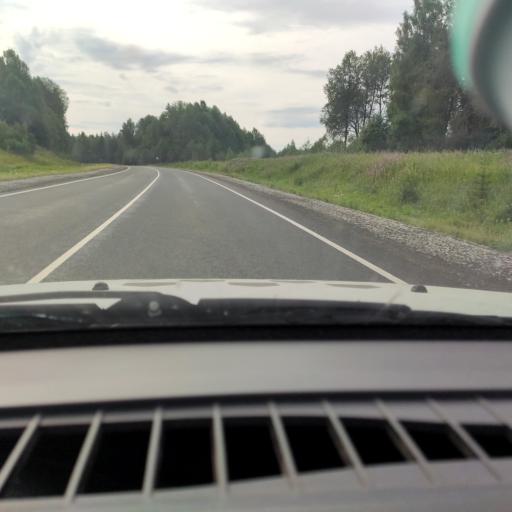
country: RU
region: Kirov
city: Kostino
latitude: 58.6422
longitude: 53.8009
